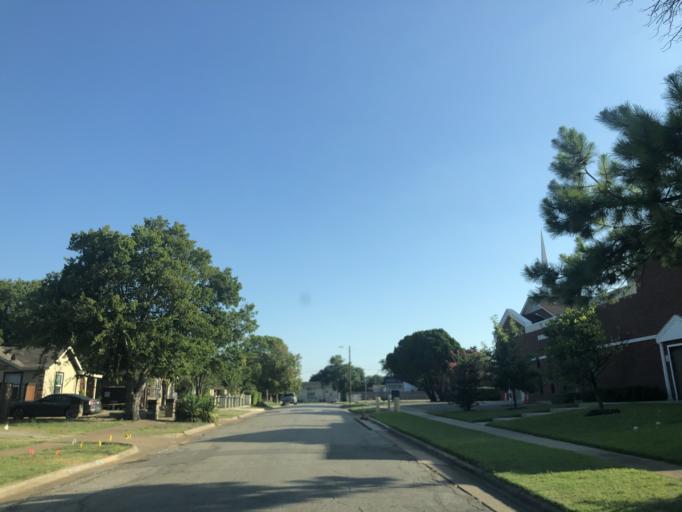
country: US
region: Texas
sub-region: Dallas County
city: Grand Prairie
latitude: 32.7334
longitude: -97.0363
